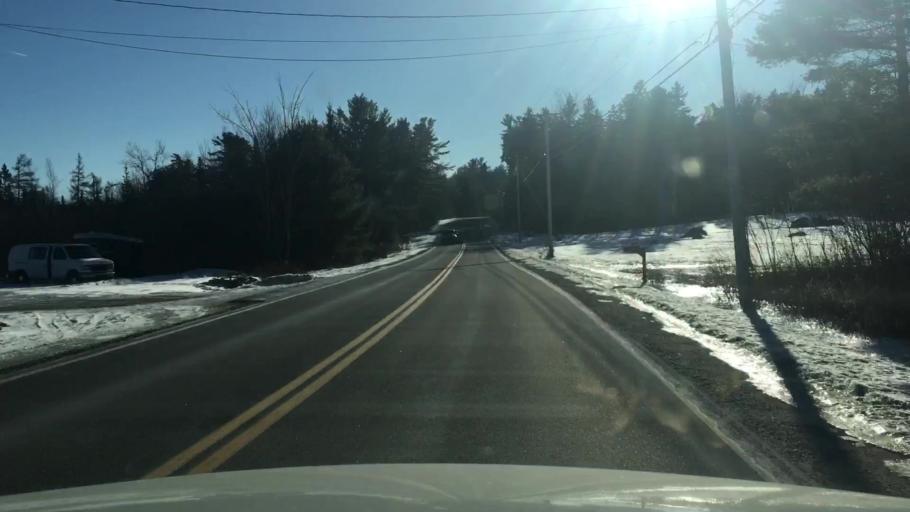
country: US
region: Maine
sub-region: Hancock County
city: Orland
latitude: 44.5191
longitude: -68.7499
